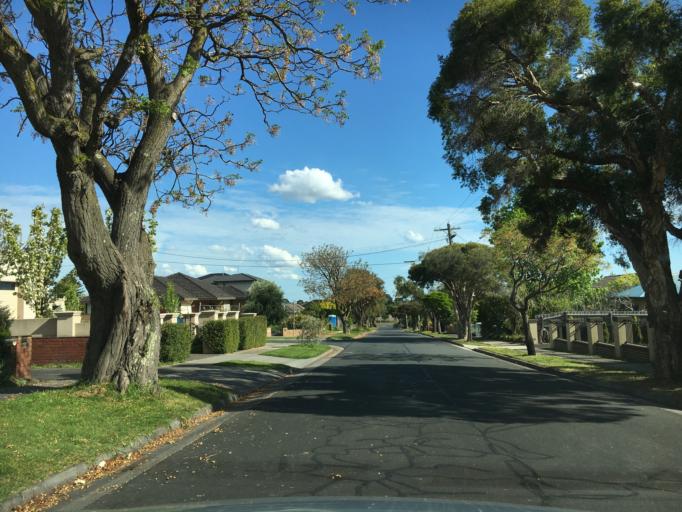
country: AU
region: Victoria
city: Clayton
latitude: -37.9056
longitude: 145.1174
